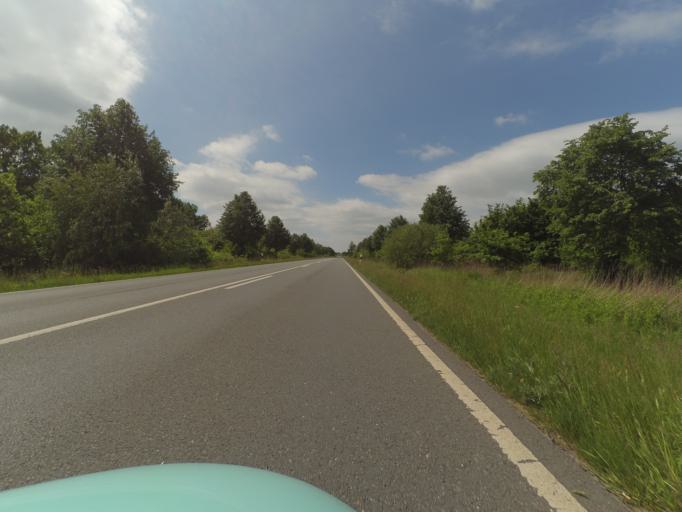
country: DE
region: Lower Saxony
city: Arpke
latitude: 52.3953
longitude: 10.0938
